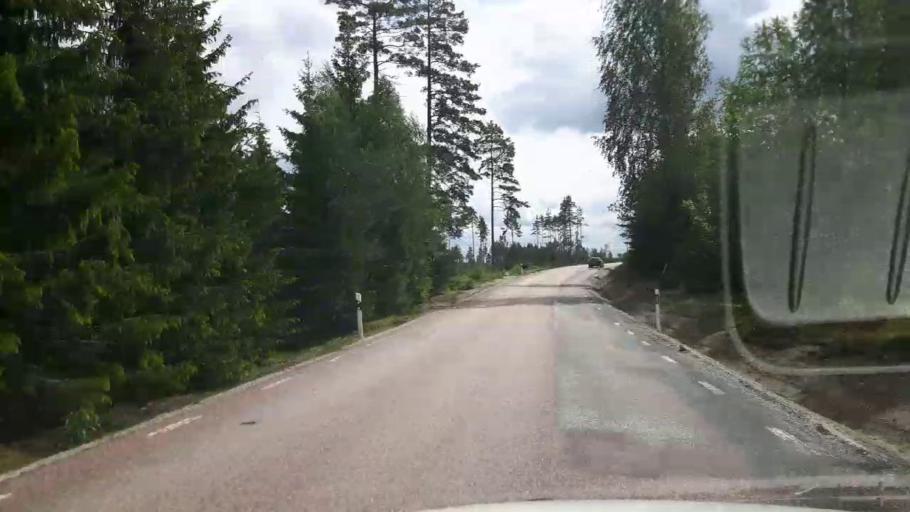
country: SE
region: Vaestmanland
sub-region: Skinnskattebergs Kommun
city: Skinnskatteberg
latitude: 59.8255
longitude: 15.8351
